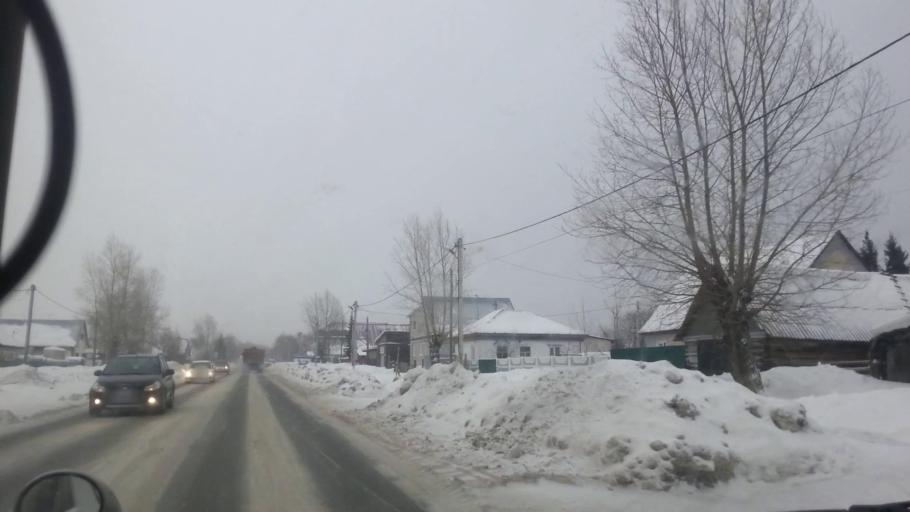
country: RU
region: Altai Krai
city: Vlasikha
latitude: 53.2975
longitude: 83.5851
